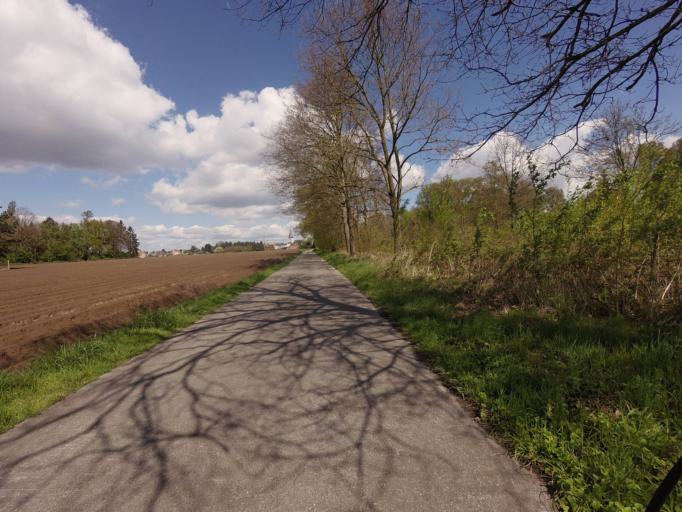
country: BE
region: Flanders
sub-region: Provincie Vlaams-Brabant
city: Zemst
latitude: 50.9565
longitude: 4.4922
